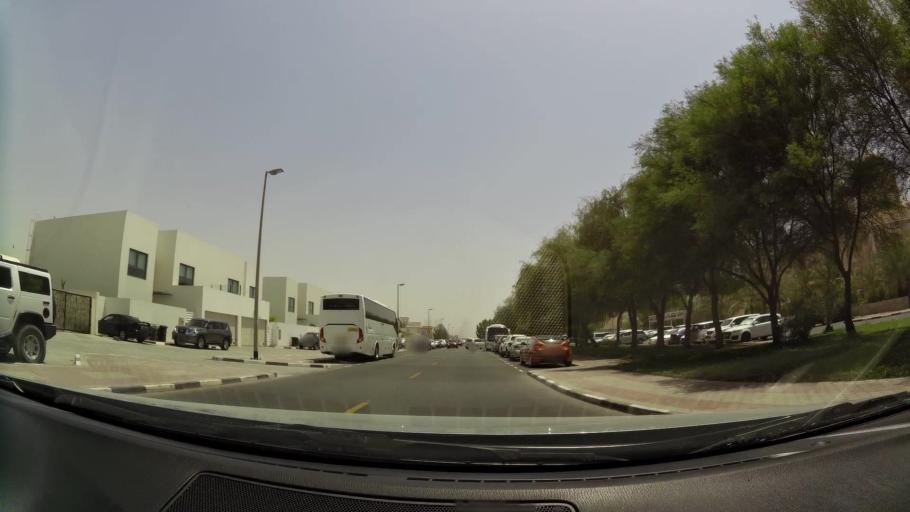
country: AE
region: Dubai
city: Dubai
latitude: 25.1373
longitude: 55.1981
